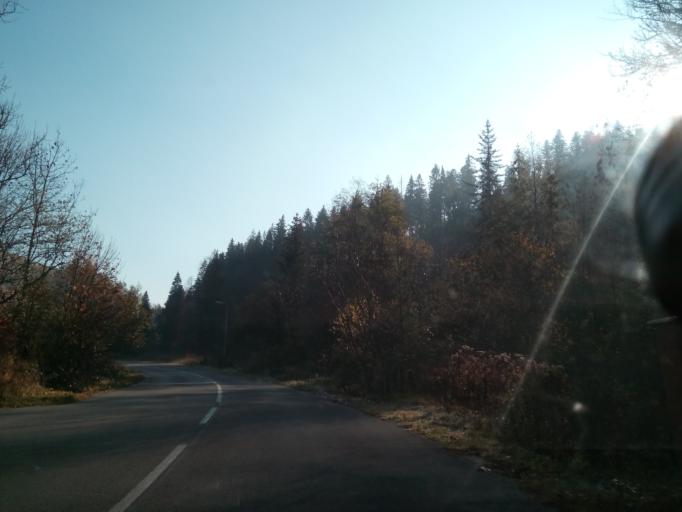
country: PL
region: Silesian Voivodeship
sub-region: Powiat zywiecki
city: Rycerka Gorna
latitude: 49.4418
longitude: 18.9237
